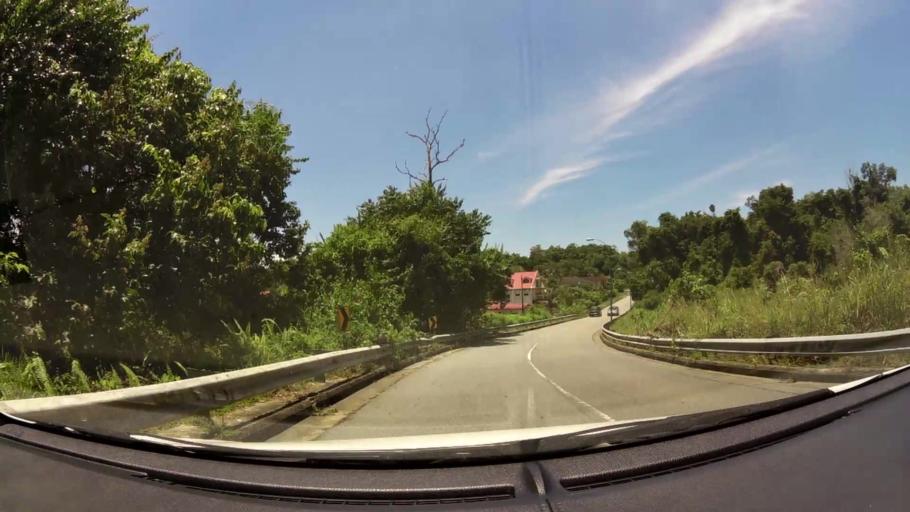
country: BN
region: Brunei and Muara
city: Bandar Seri Begawan
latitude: 4.9294
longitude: 114.9591
